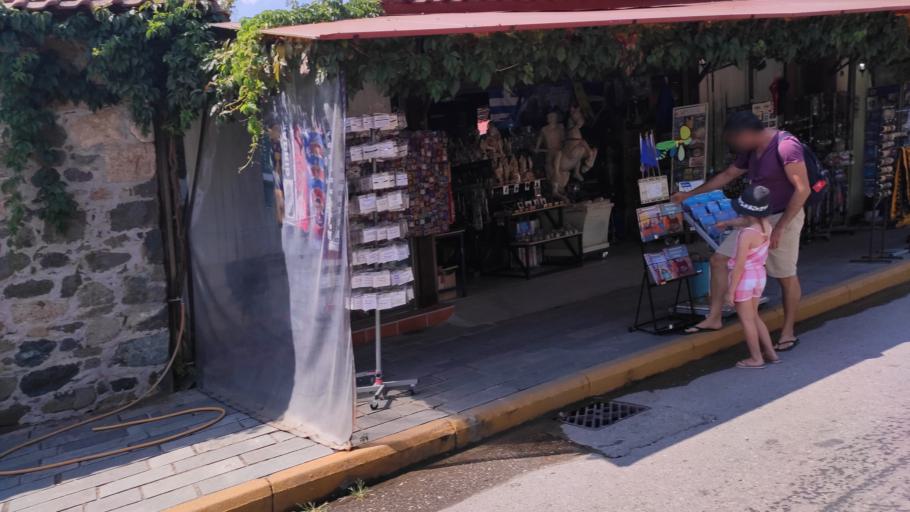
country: GR
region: Central Macedonia
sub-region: Nomos Imathias
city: Vergina
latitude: 40.4859
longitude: 22.3210
